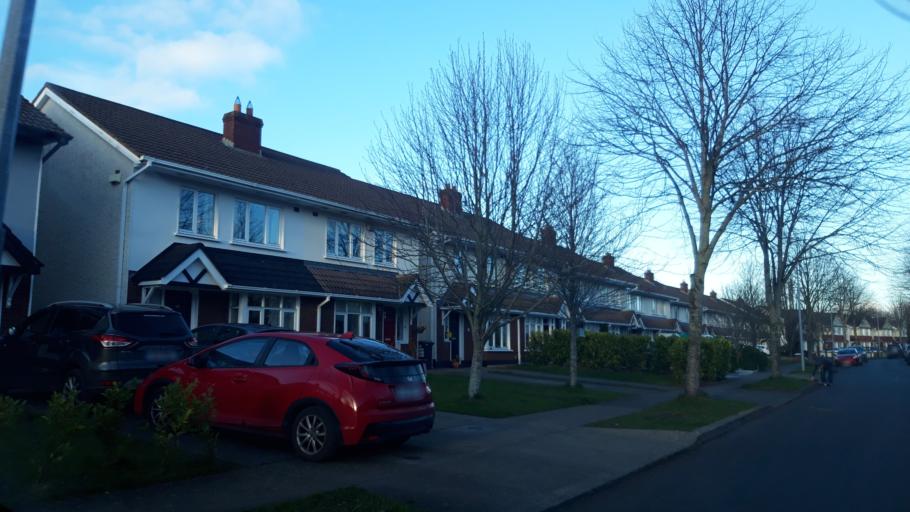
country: IE
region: Leinster
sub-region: Fingal County
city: Blanchardstown
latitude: 53.3735
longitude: -6.3927
